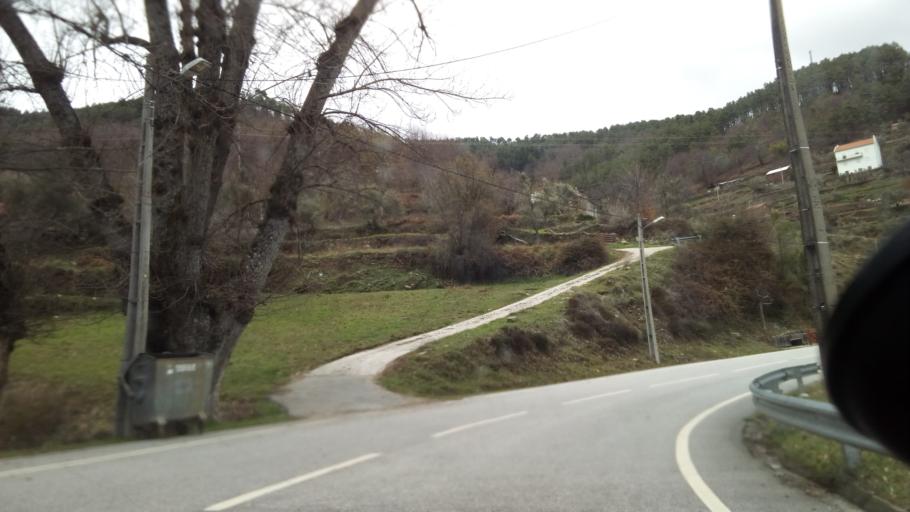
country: PT
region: Guarda
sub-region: Manteigas
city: Manteigas
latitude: 40.4062
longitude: -7.5353
